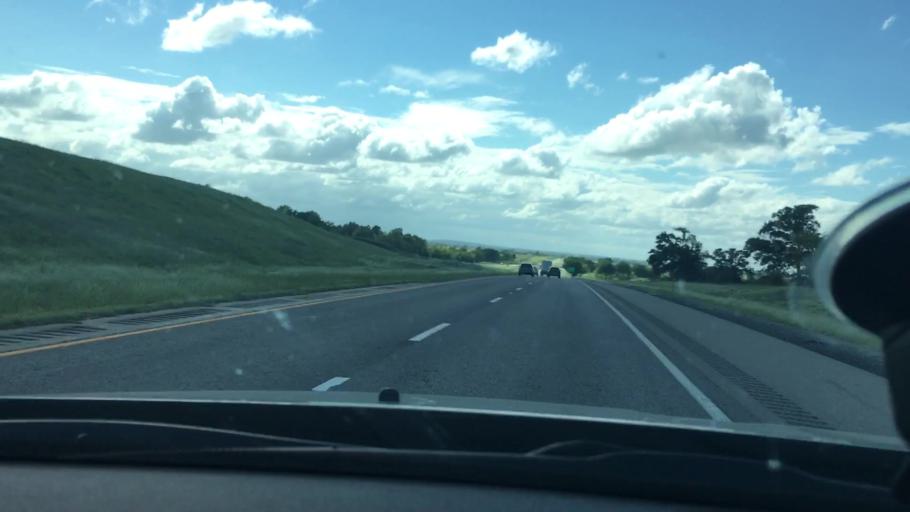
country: US
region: Oklahoma
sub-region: McIntosh County
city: Checotah
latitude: 35.4581
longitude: -95.4238
